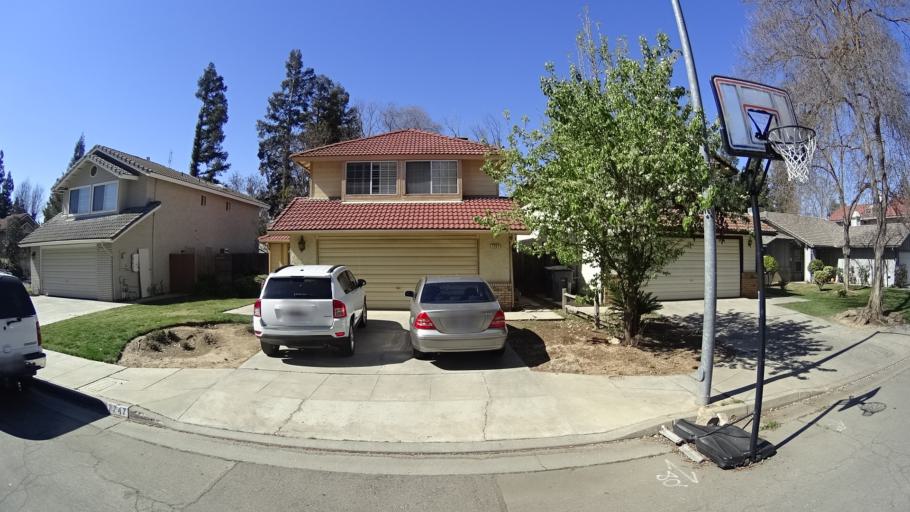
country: US
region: California
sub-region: Fresno County
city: Clovis
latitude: 36.8491
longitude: -119.7617
